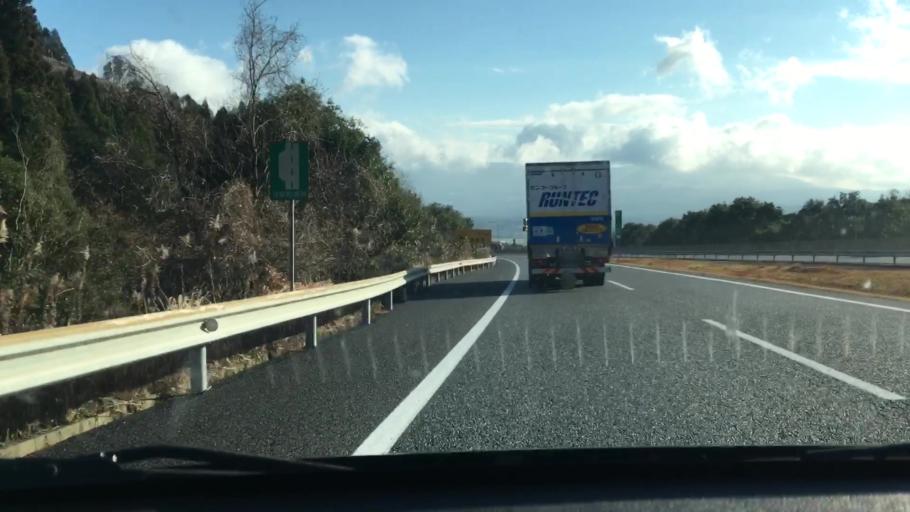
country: JP
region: Kumamoto
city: Hitoyoshi
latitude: 32.0745
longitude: 130.7931
